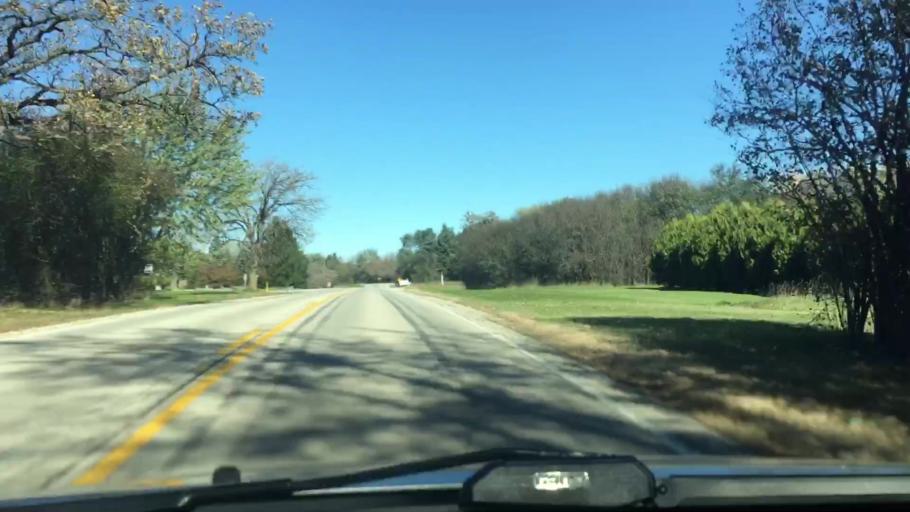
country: US
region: Wisconsin
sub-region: Waukesha County
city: North Prairie
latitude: 42.9633
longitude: -88.4048
